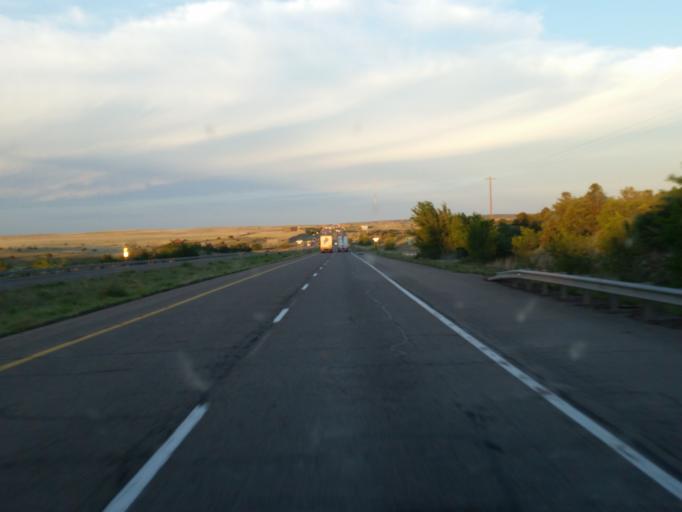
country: US
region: New Mexico
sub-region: San Miguel County
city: Las Vegas
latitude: 34.9923
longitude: -105.3137
